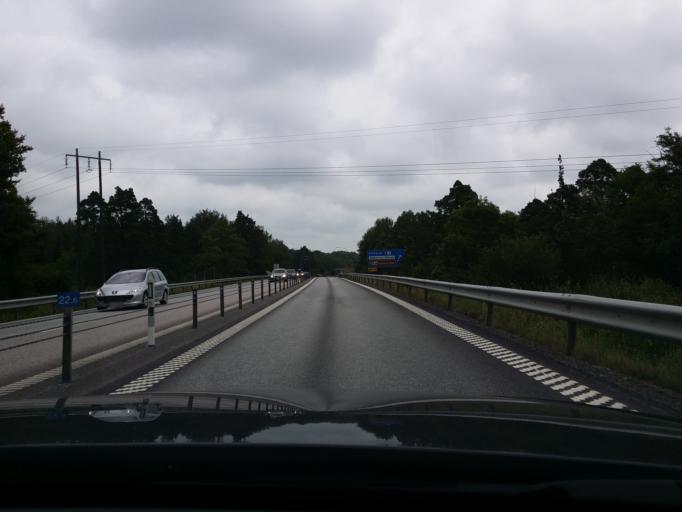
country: SE
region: Blekinge
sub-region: Karlshamns Kommun
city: Morrum
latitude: 56.1801
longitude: 14.7641
